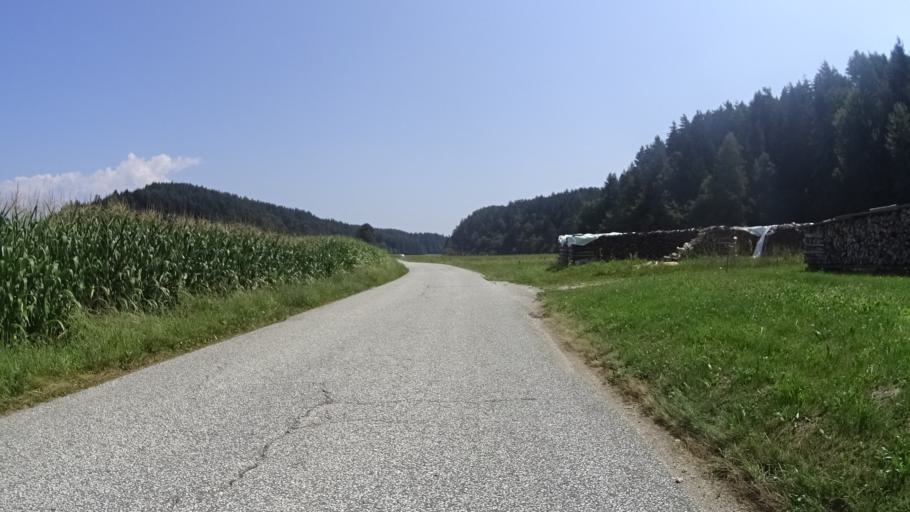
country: AT
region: Carinthia
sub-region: Politischer Bezirk Volkermarkt
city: Globasnitz
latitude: 46.5594
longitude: 14.6763
